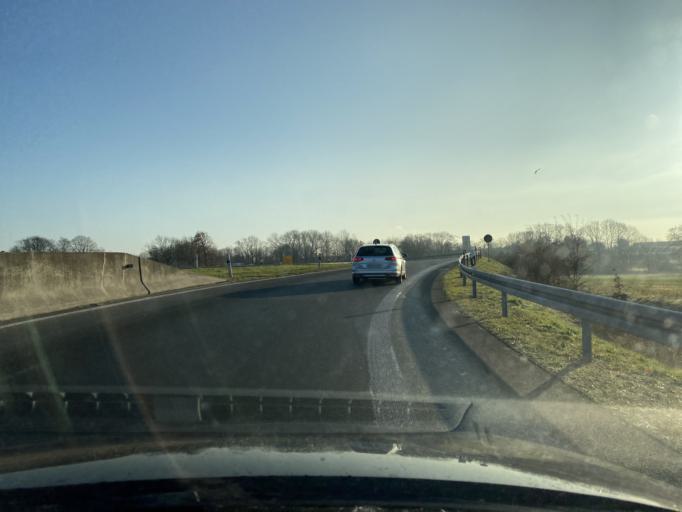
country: DE
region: North Rhine-Westphalia
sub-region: Regierungsbezirk Munster
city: Beckum
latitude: 51.7783
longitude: 8.0298
